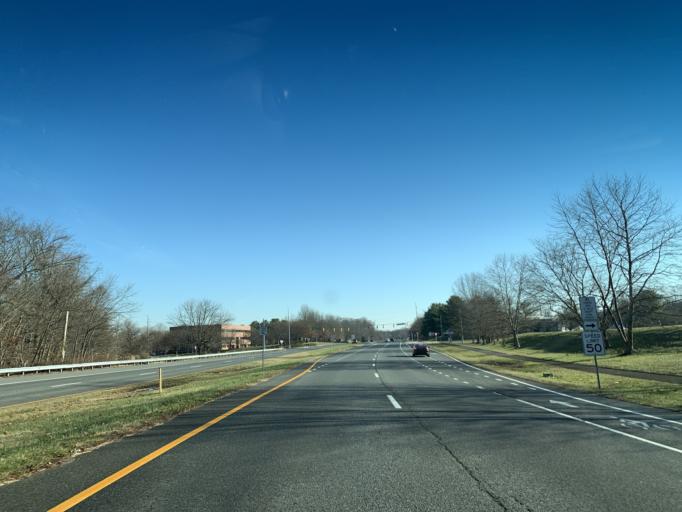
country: US
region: Delaware
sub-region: New Castle County
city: Pike Creek Valley
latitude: 39.6951
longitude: -75.6657
